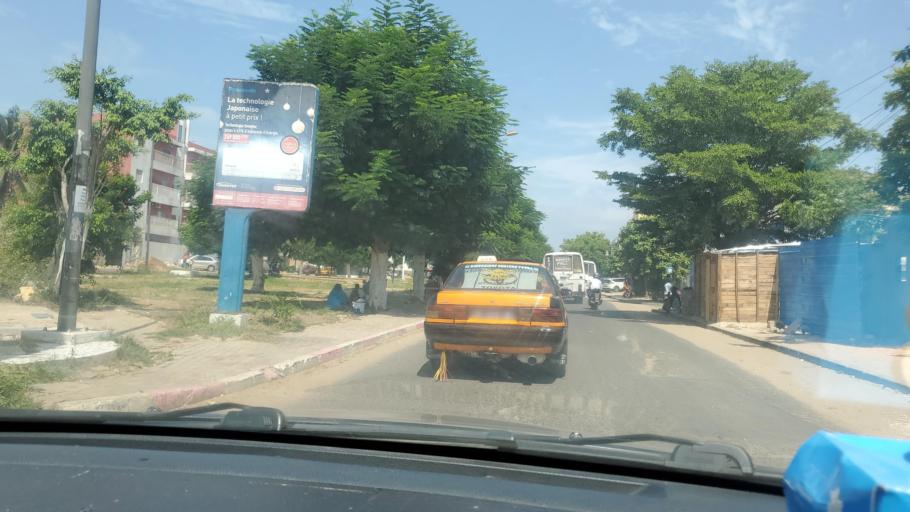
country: SN
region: Dakar
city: Grand Dakar
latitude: 14.7148
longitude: -17.4551
